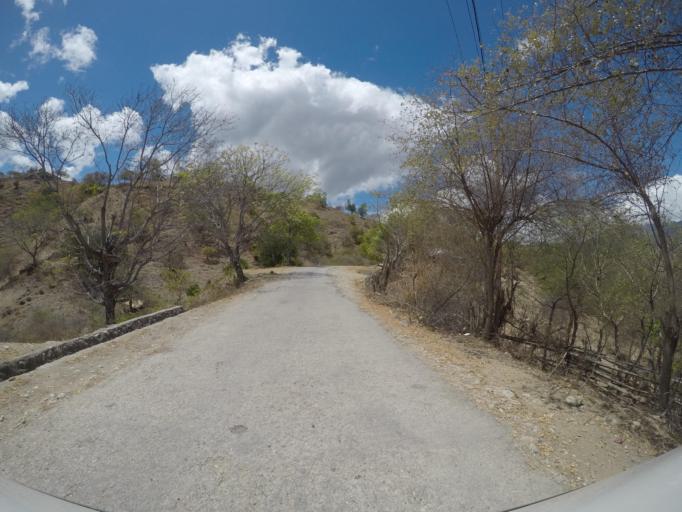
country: TL
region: Baucau
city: Baucau
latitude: -8.4807
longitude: 126.6065
